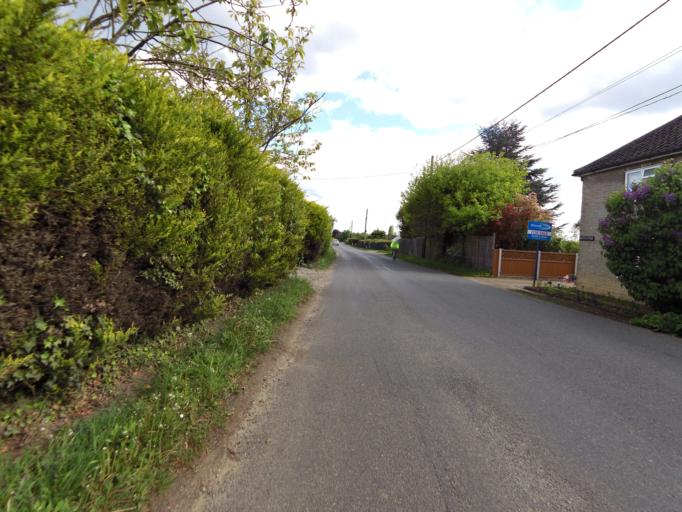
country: GB
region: England
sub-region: Suffolk
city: Elmswell
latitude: 52.2103
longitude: 0.9168
